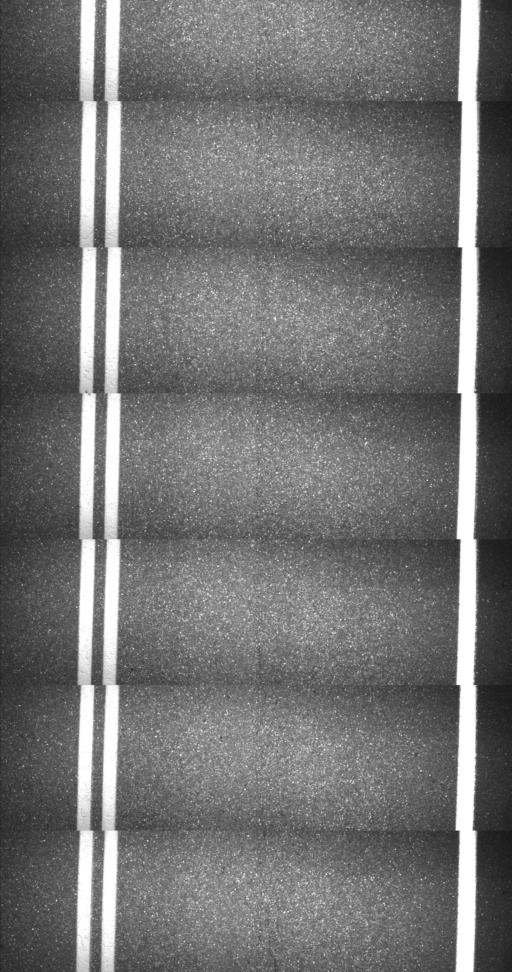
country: US
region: Massachusetts
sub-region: Franklin County
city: Colrain
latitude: 42.7828
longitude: -72.8078
